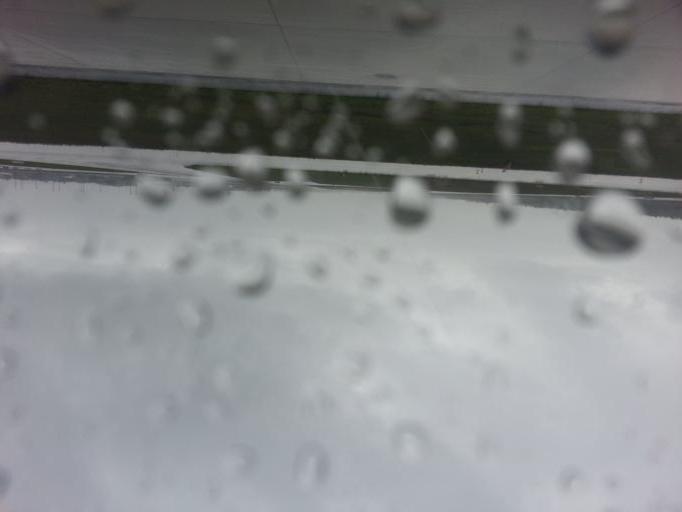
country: NO
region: Akershus
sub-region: Ullensaker
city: Jessheim
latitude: 60.2015
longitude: 11.1200
